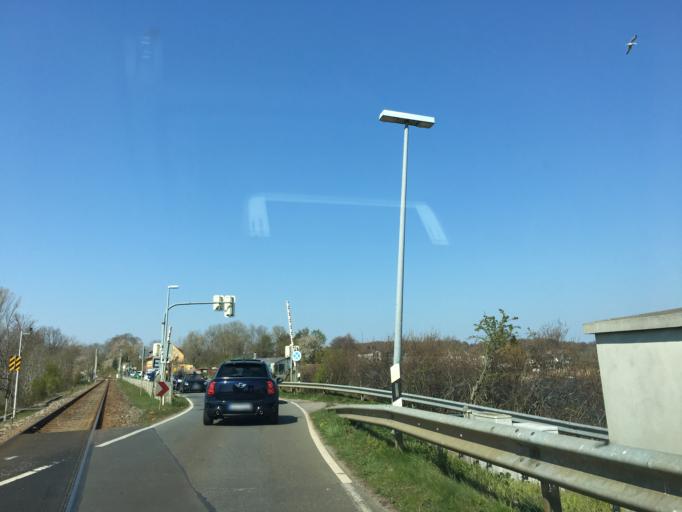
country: DE
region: Schleswig-Holstein
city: Dollrottfeld
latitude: 54.5840
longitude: 9.8196
